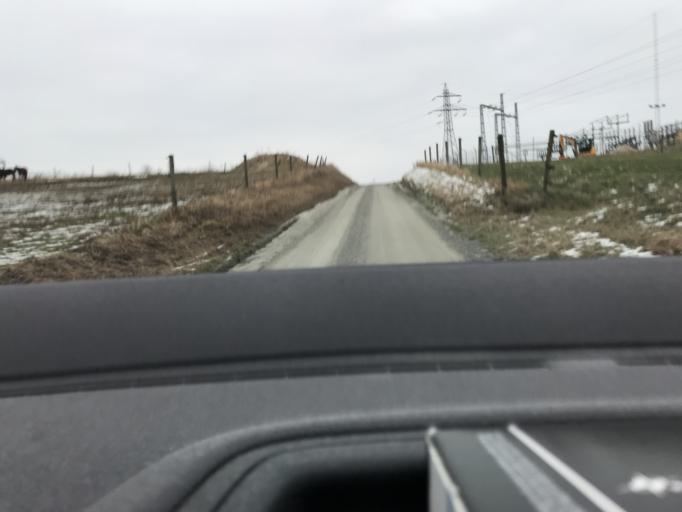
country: SE
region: Skane
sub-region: Ystads Kommun
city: Kopingebro
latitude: 55.4599
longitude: 13.8930
